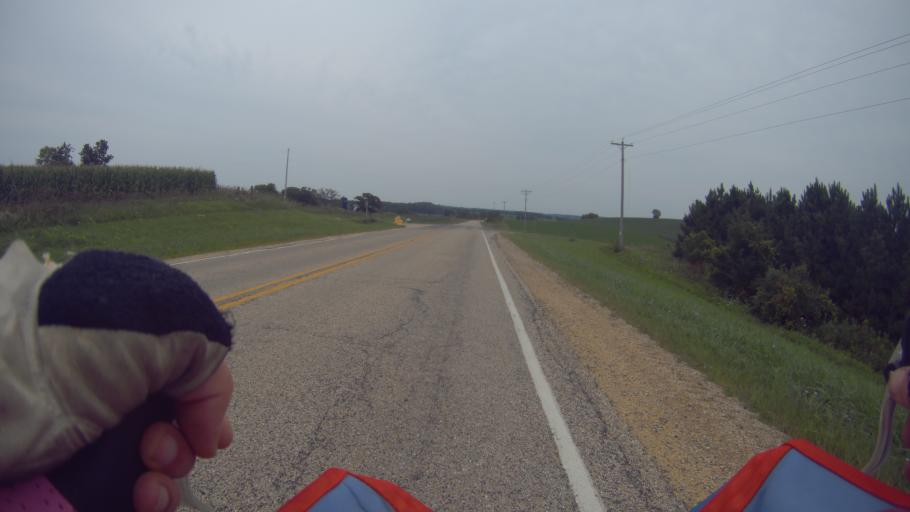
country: US
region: Wisconsin
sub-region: Dane County
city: Belleville
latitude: 42.9080
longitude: -89.5684
